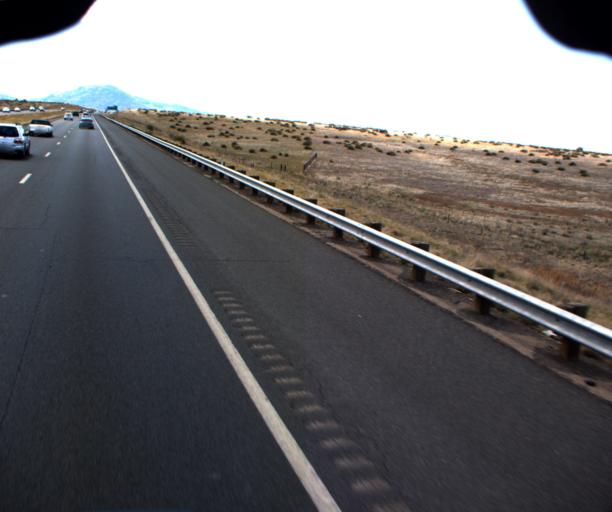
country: US
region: Arizona
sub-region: Yavapai County
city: Prescott Valley
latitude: 34.6308
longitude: -112.3781
